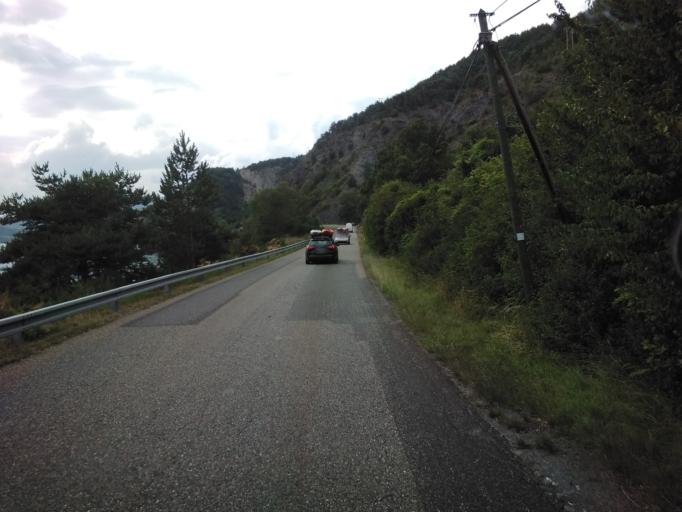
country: FR
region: Provence-Alpes-Cote d'Azur
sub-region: Departement des Alpes-de-Haute-Provence
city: Seyne-les-Alpes
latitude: 44.4603
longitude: 6.3743
